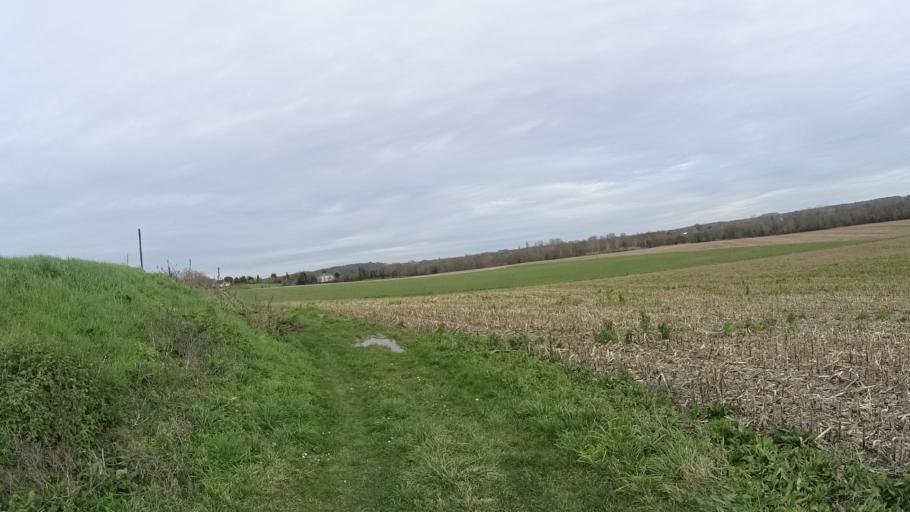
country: FR
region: Aquitaine
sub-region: Departement de la Dordogne
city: Saint-Aulaye
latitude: 45.2593
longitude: 0.1671
